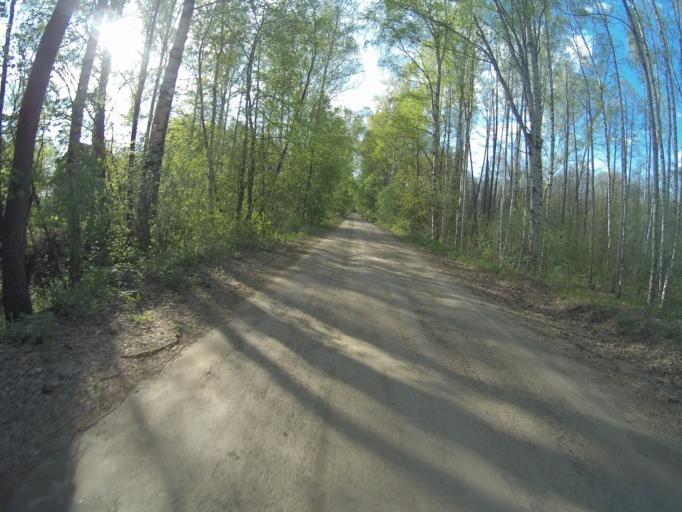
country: RU
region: Vladimir
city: Raduzhnyy
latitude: 56.0044
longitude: 40.2640
